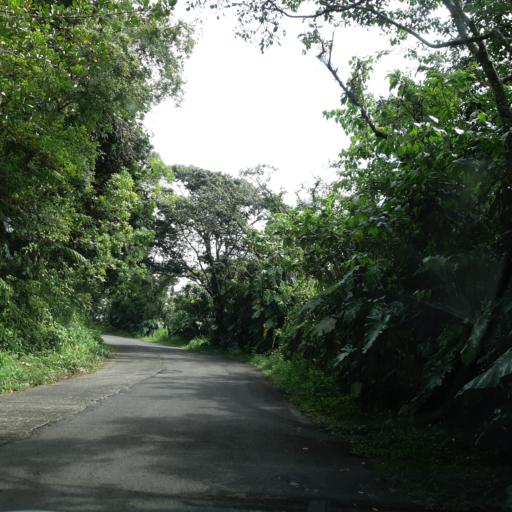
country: GP
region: Guadeloupe
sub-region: Guadeloupe
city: Saint-Claude
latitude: 16.0327
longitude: -61.6808
